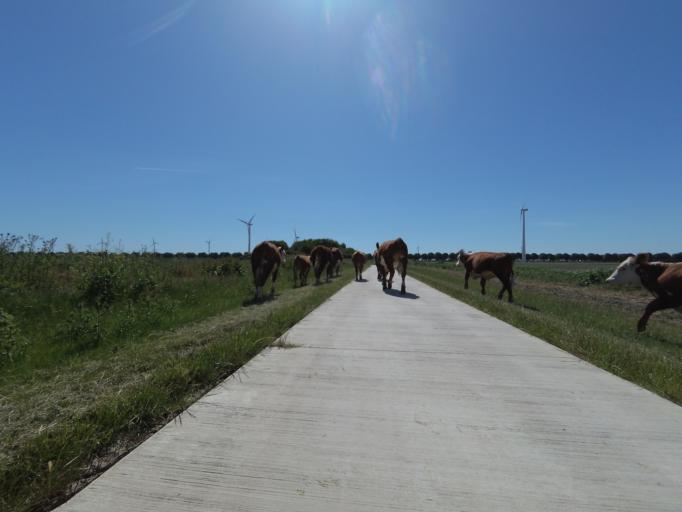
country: NL
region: Utrecht
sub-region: Gemeente Bunschoten
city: Spakenburg
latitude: 52.3386
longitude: 5.4120
